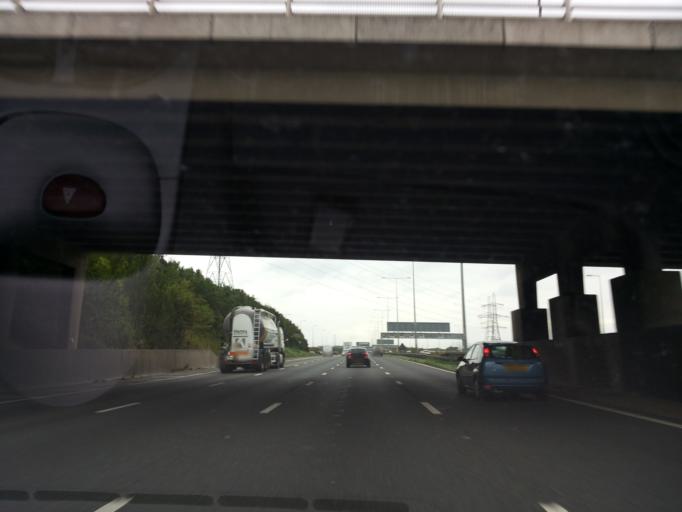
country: GB
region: England
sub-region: Kent
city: Swanscombe
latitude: 51.4266
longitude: 0.3306
